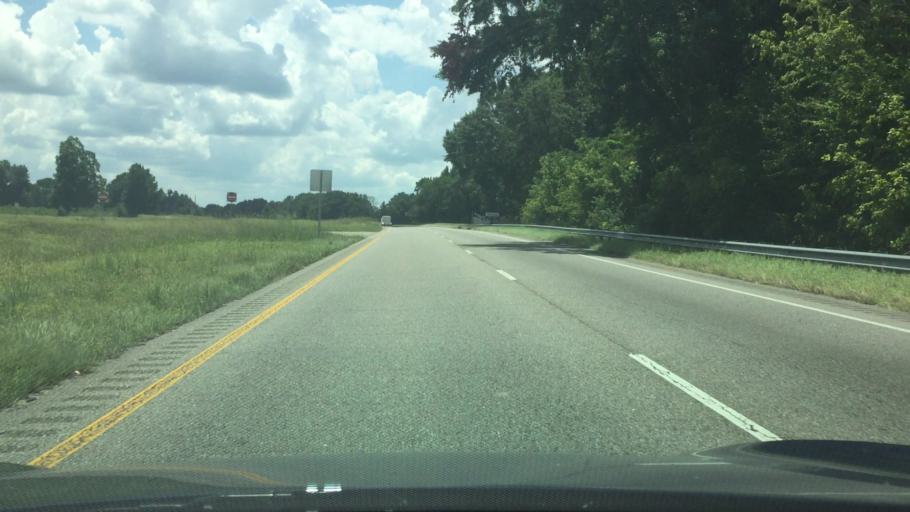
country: US
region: Alabama
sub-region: Montgomery County
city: Taylor
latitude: 32.0778
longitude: -86.0635
